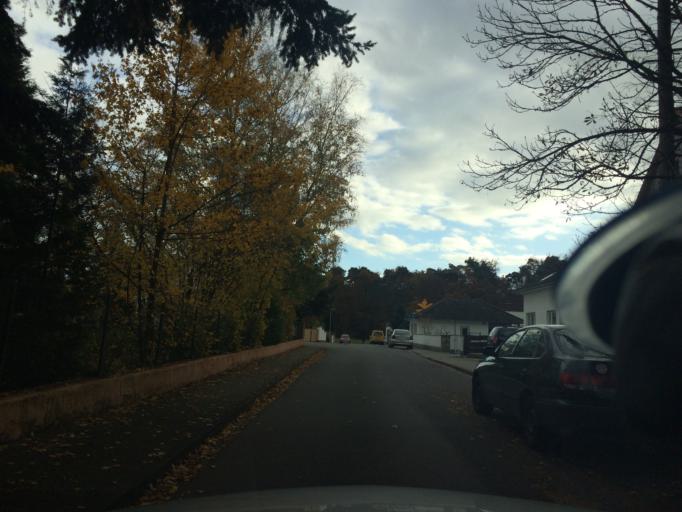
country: DE
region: Hesse
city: Morfelden-Walldorf
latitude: 49.9723
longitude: 8.5531
